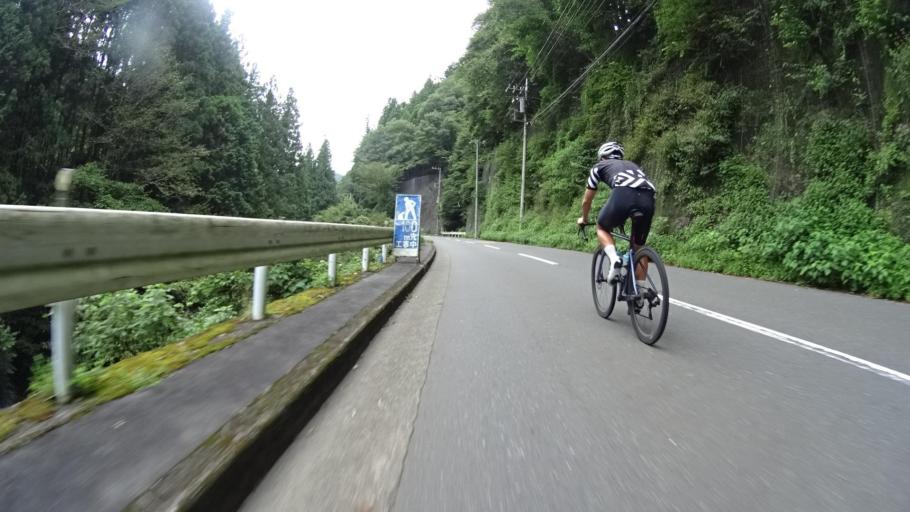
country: JP
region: Yamanashi
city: Uenohara
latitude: 35.7084
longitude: 139.0960
